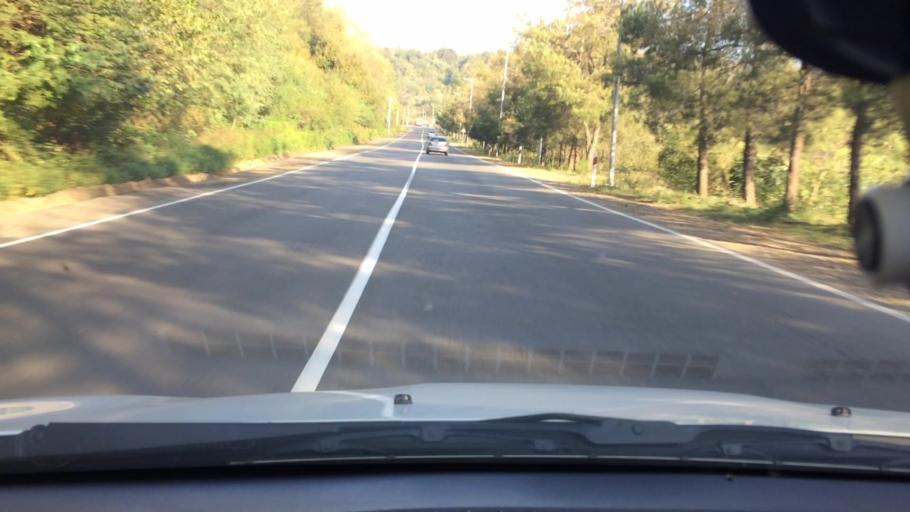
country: GE
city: Shorapani
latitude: 42.0965
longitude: 43.0759
